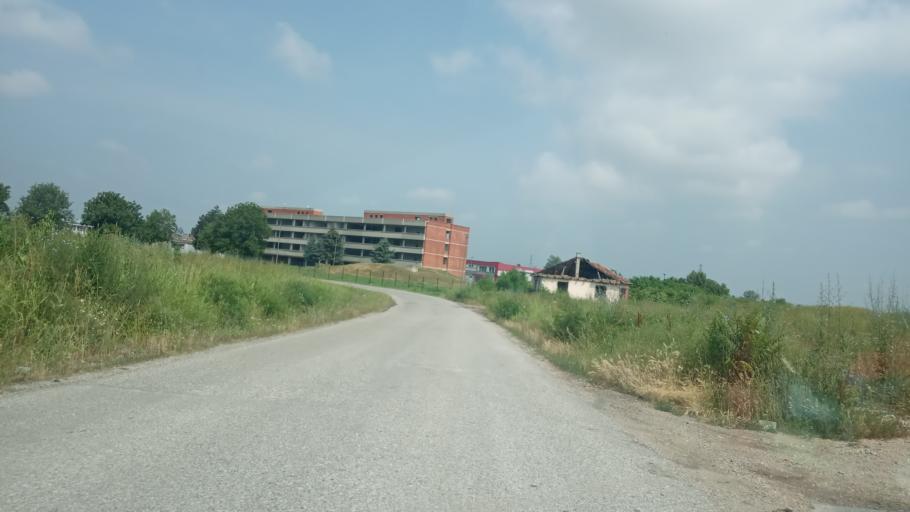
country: RS
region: Central Serbia
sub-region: Belgrade
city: Palilula
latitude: 44.8443
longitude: 20.5086
